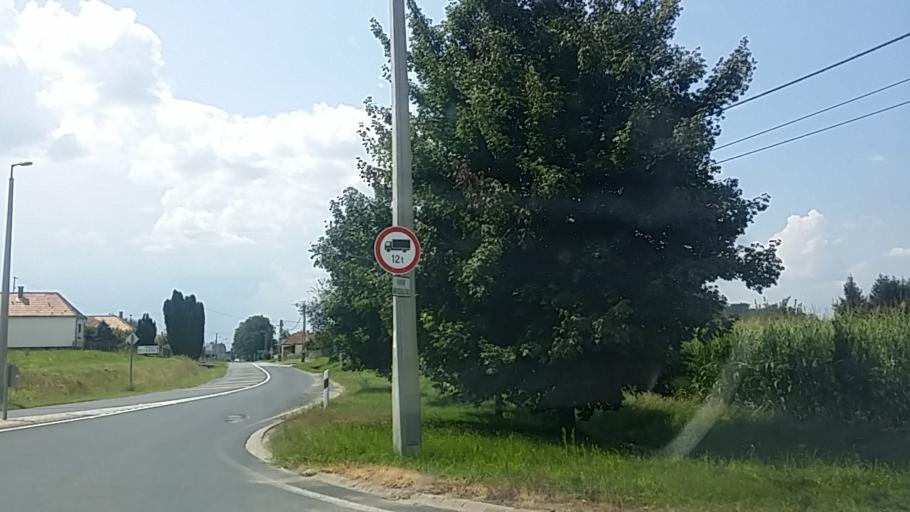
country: HR
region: Medimurska
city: Podturen
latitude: 46.5160
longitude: 16.5617
